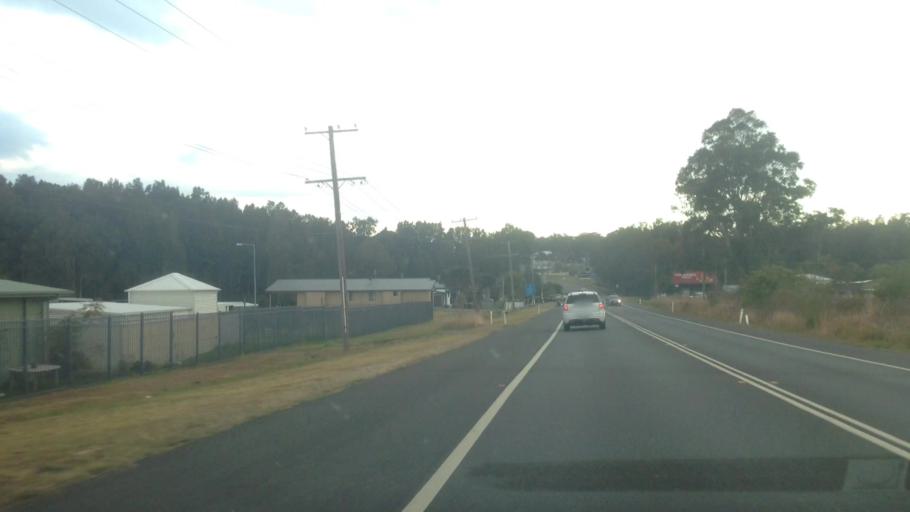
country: AU
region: New South Wales
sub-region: Wyong Shire
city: Tuggerawong
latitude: -33.2638
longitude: 151.4758
